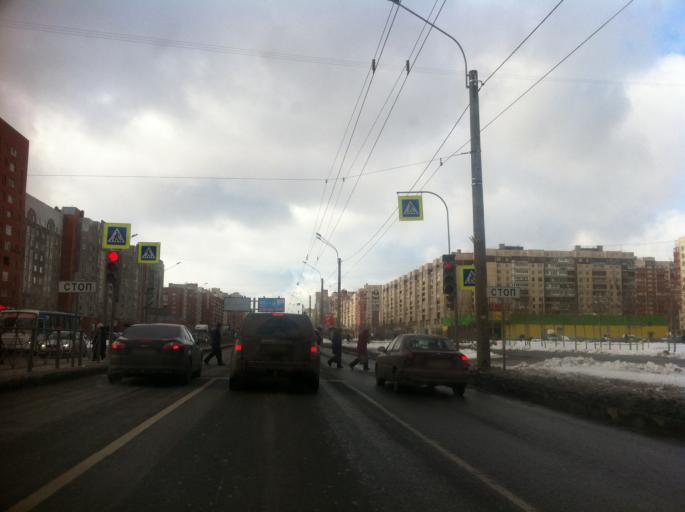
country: RU
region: St.-Petersburg
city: Dachnoye
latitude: 59.8528
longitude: 30.2177
